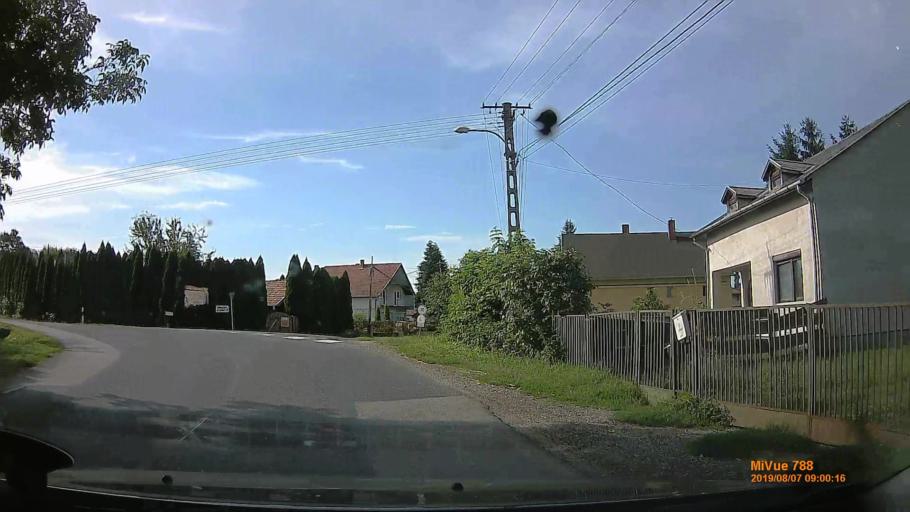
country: HU
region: Zala
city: Pacsa
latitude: 46.7292
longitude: 16.9455
